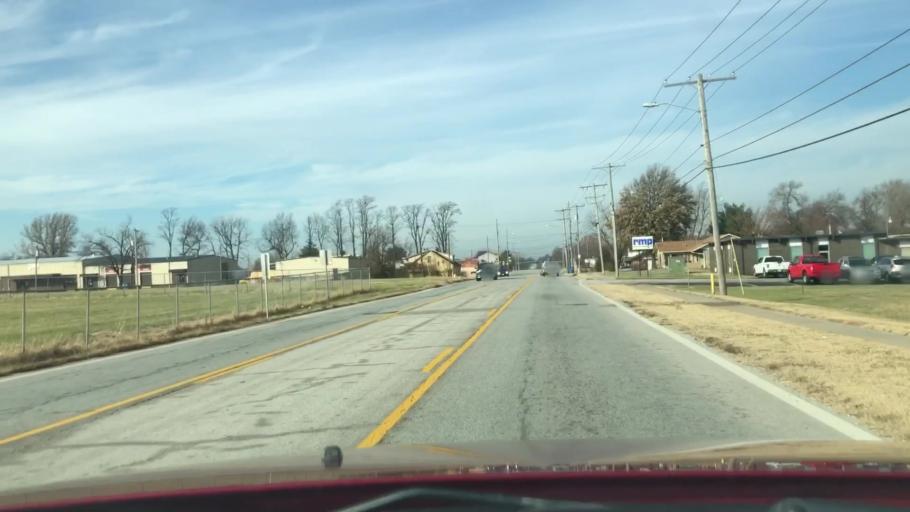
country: US
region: Missouri
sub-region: Greene County
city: Springfield
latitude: 37.2254
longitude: -93.2563
